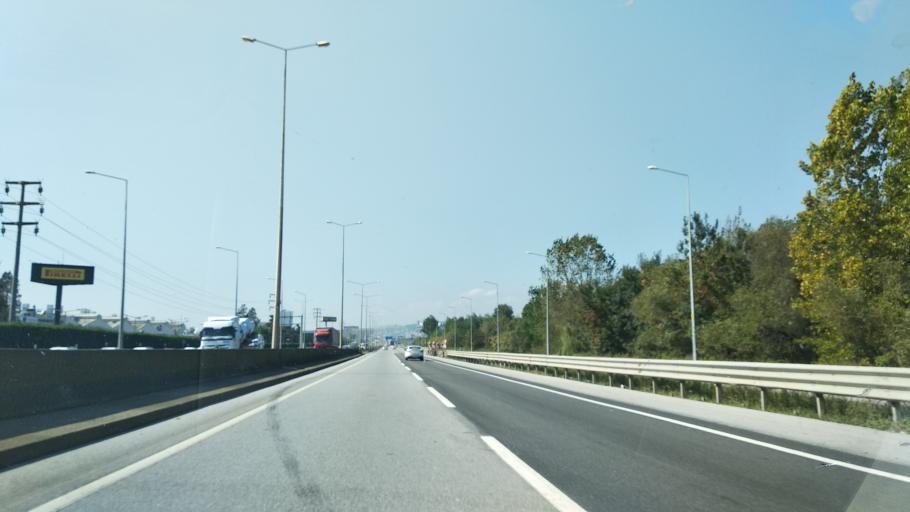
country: TR
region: Kocaeli
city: Kosekoy
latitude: 40.7565
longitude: 30.0022
